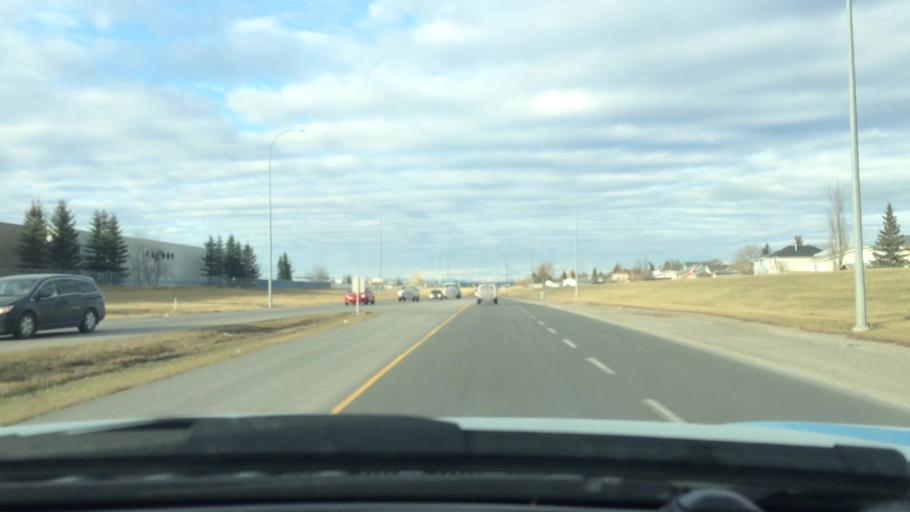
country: CA
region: Alberta
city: Calgary
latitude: 51.0150
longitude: -113.9649
